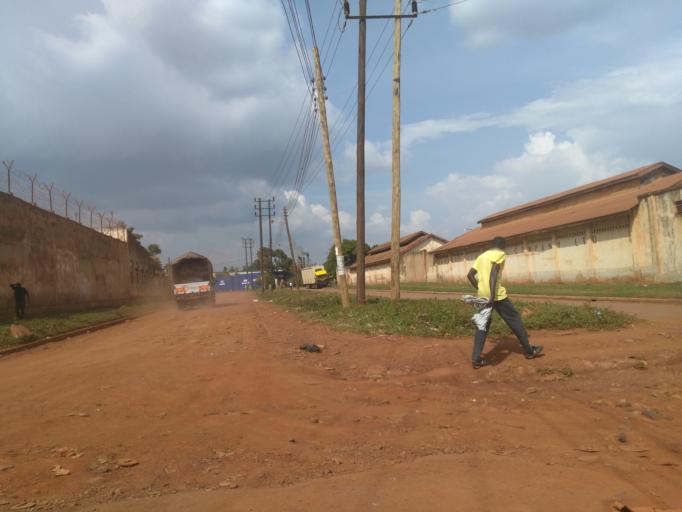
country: UG
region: Eastern Region
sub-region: Jinja District
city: Jinja
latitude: 0.4279
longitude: 33.2166
